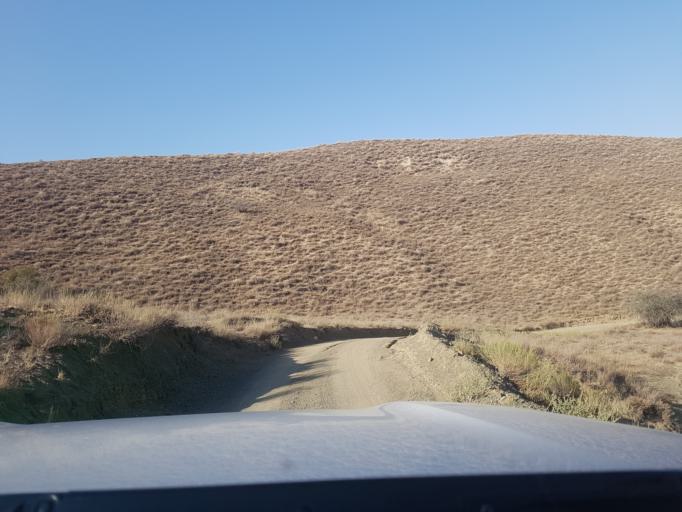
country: TM
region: Balkan
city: Magtymguly
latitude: 38.2998
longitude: 56.7841
